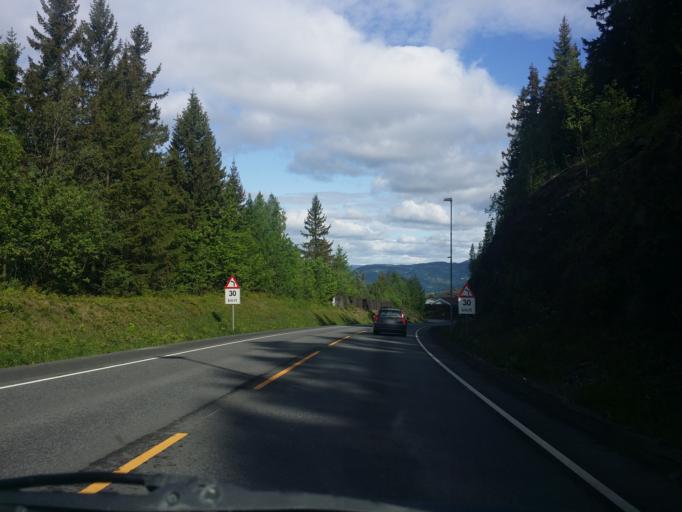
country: NO
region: Oppland
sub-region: Lillehammer
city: Lillehammer
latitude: 61.1020
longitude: 10.5014
